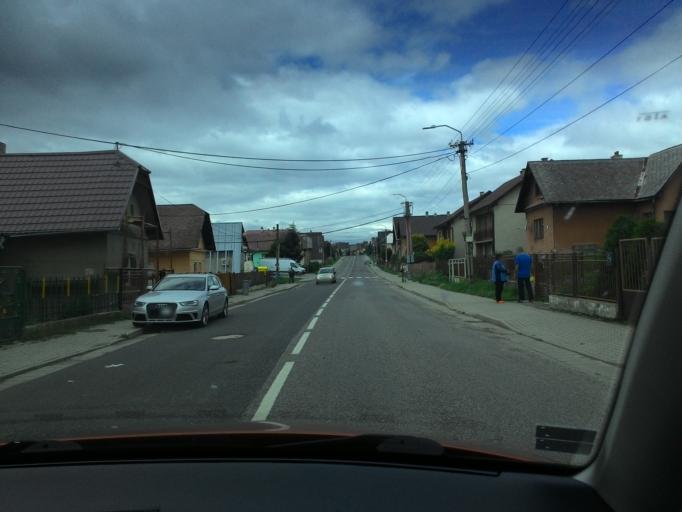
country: SK
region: Zilinsky
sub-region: Okres Liptovsky Mikulas
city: Hybe
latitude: 49.0579
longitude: 19.8840
